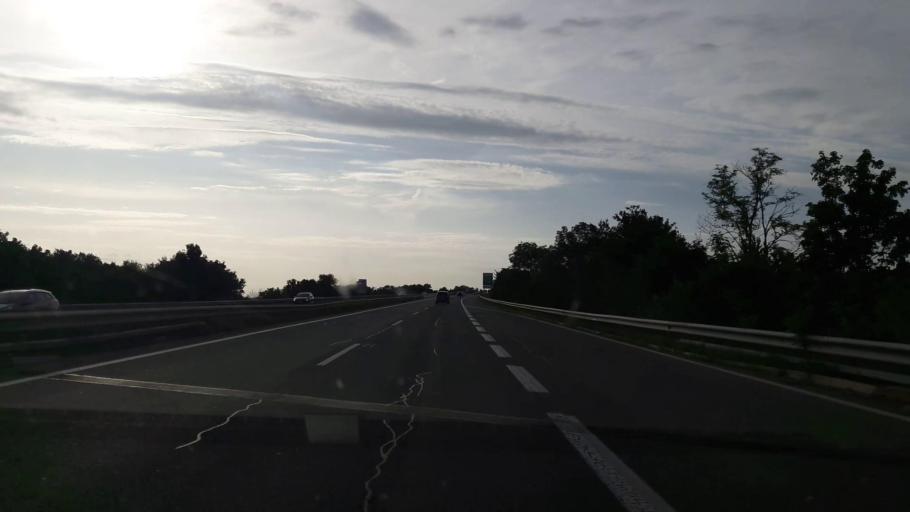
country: AT
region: Burgenland
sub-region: Eisenstadt-Umgebung
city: Mullendorf
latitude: 47.8350
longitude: 16.4491
